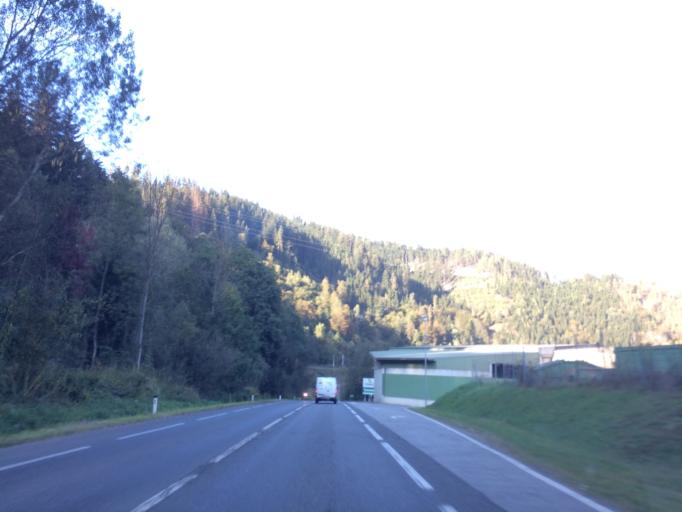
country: AT
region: Styria
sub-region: Politischer Bezirk Leoben
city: Sankt Michael in Obersteiermark
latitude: 47.3367
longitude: 15.0289
